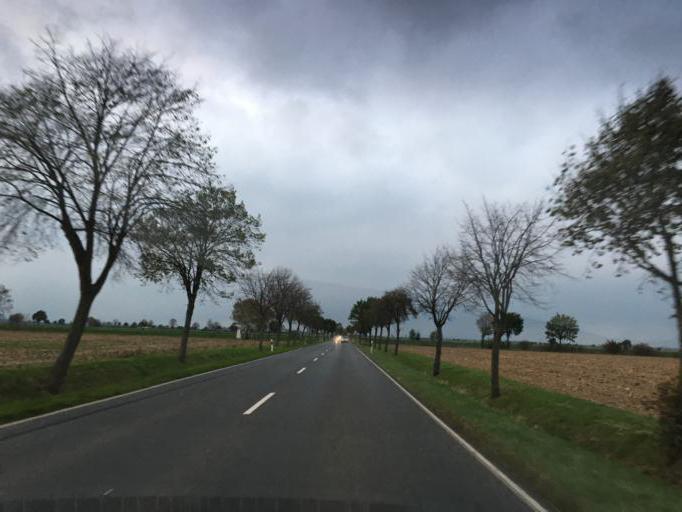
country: DE
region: North Rhine-Westphalia
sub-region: Regierungsbezirk Koln
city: Vettweiss
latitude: 50.7426
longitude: 6.5863
